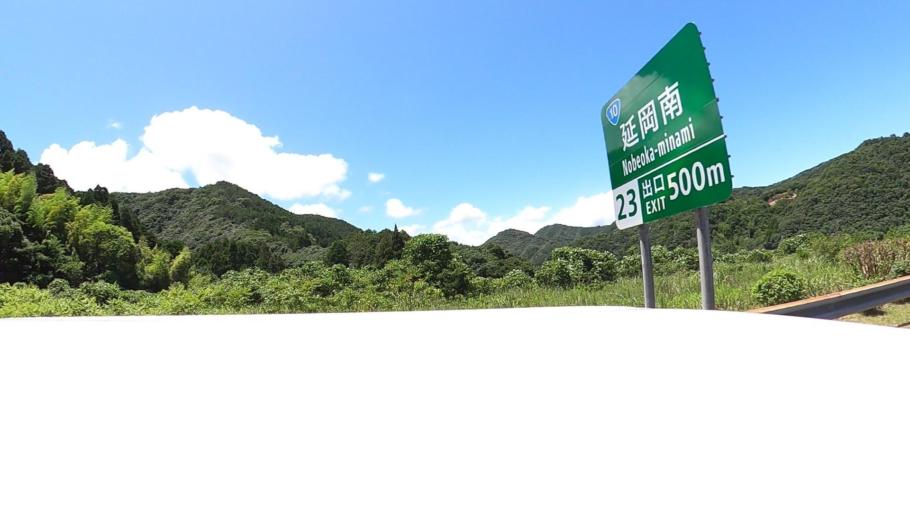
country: JP
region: Miyazaki
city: Nobeoka
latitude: 32.5214
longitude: 131.6649
